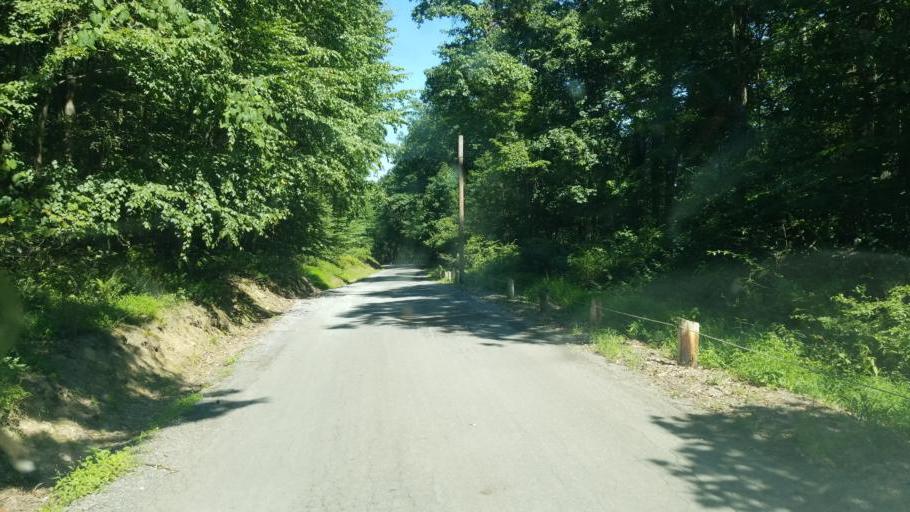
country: US
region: Pennsylvania
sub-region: Clarion County
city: Clarion
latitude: 41.1863
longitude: -79.4338
